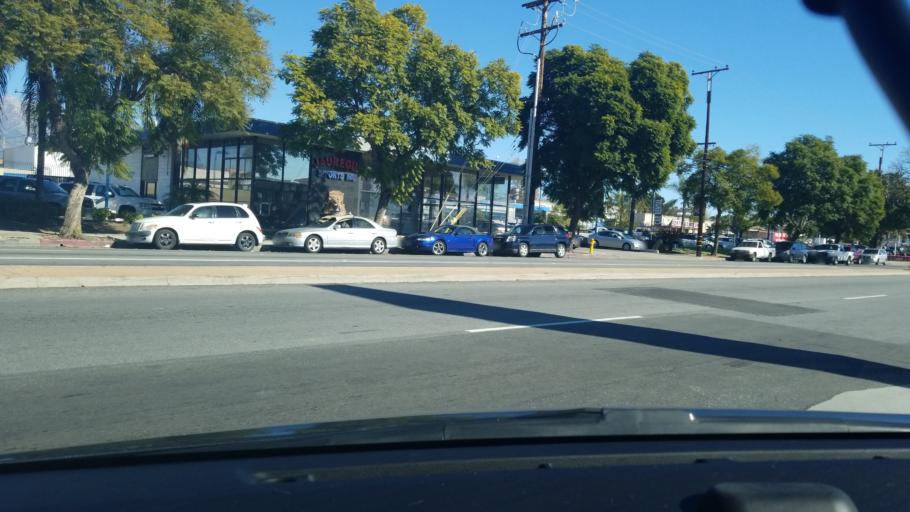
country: US
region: California
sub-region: San Bernardino County
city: Ontario
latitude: 34.0632
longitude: -117.6696
